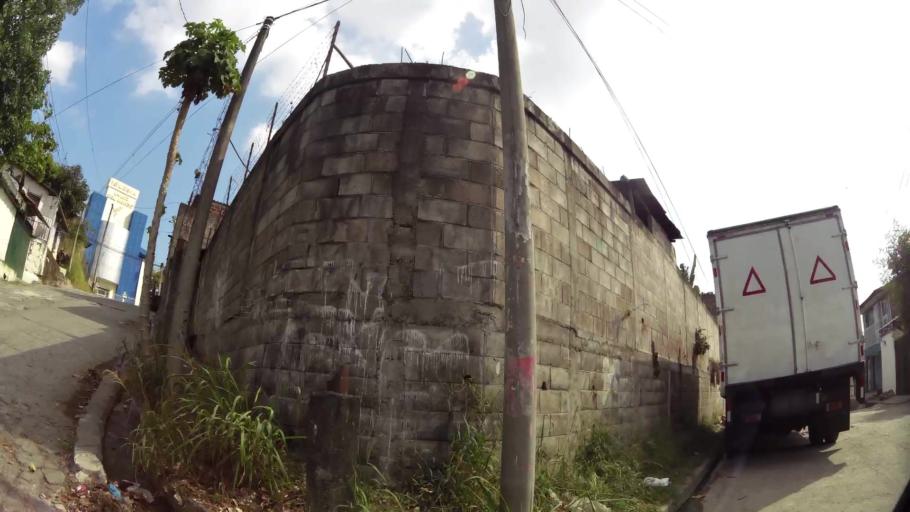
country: SV
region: San Salvador
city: Delgado
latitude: 13.7218
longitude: -89.1632
